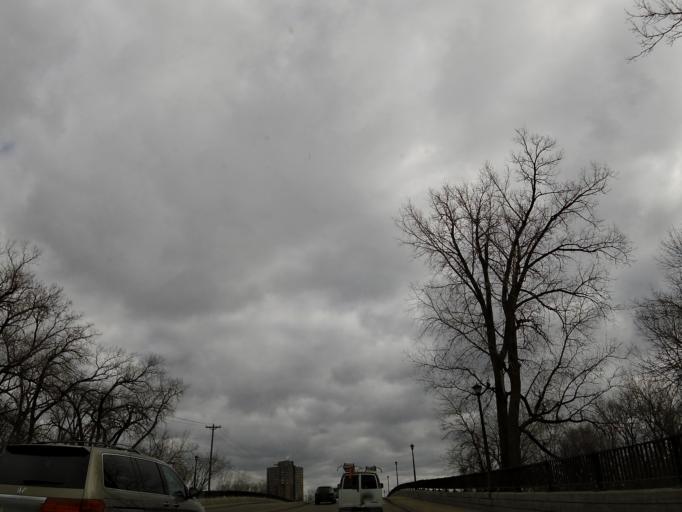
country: US
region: Minnesota
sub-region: Hennepin County
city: Saint Louis Park
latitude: 44.9484
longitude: -93.3248
